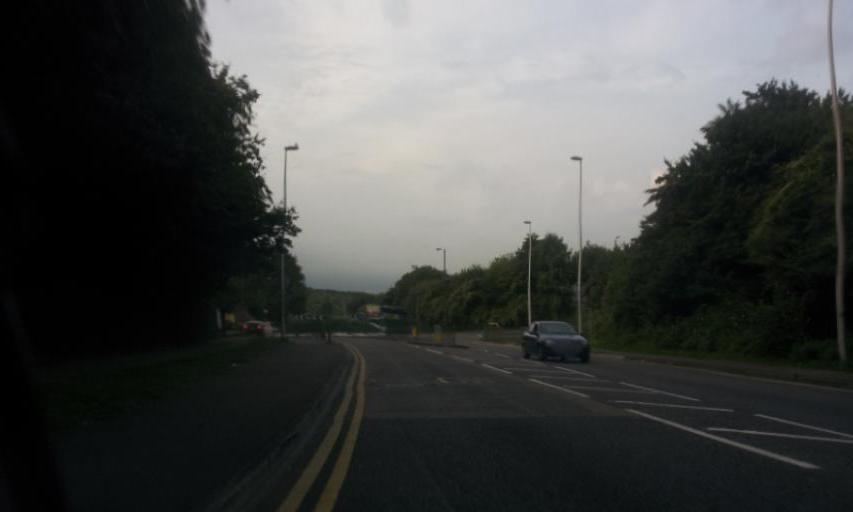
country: GB
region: England
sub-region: Kent
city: Chatham
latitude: 51.3517
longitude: 0.5350
